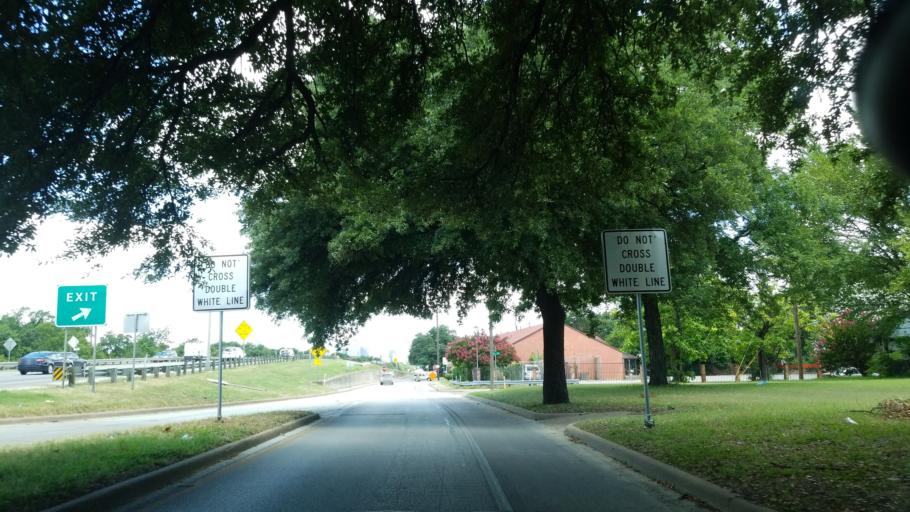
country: US
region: Texas
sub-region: Dallas County
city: Dallas
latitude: 32.7522
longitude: -96.7632
